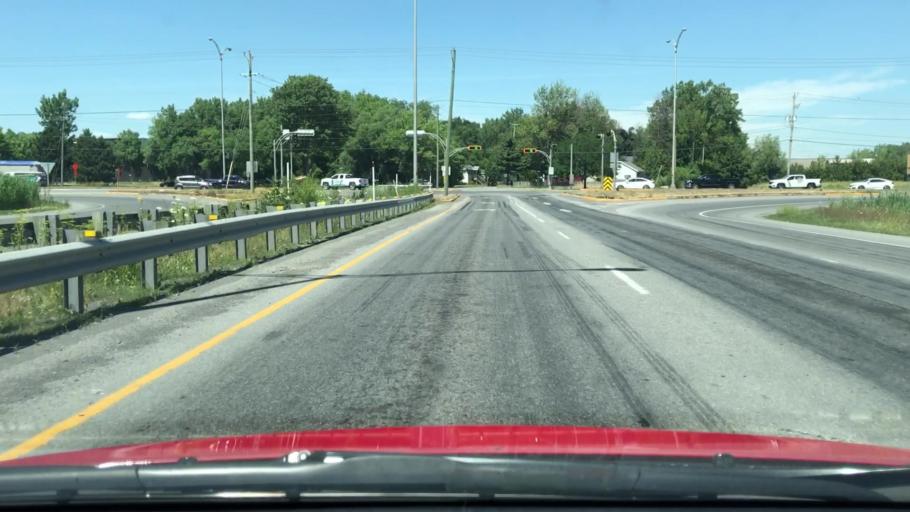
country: CA
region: Quebec
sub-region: Monteregie
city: Saint-Constant
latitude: 45.3944
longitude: -73.6033
